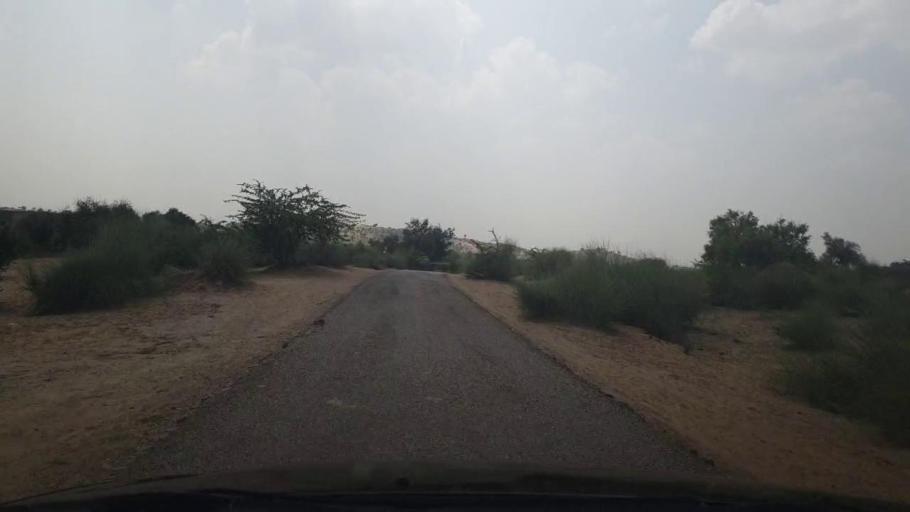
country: PK
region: Sindh
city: Islamkot
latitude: 24.9944
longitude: 70.4966
